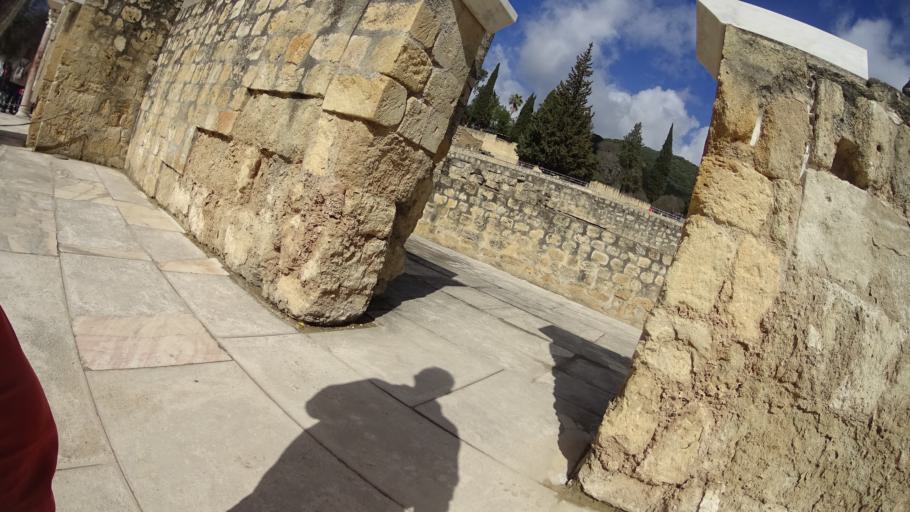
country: ES
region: Andalusia
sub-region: Province of Cordoba
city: Villarrubia
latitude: 37.8864
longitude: -4.8679
